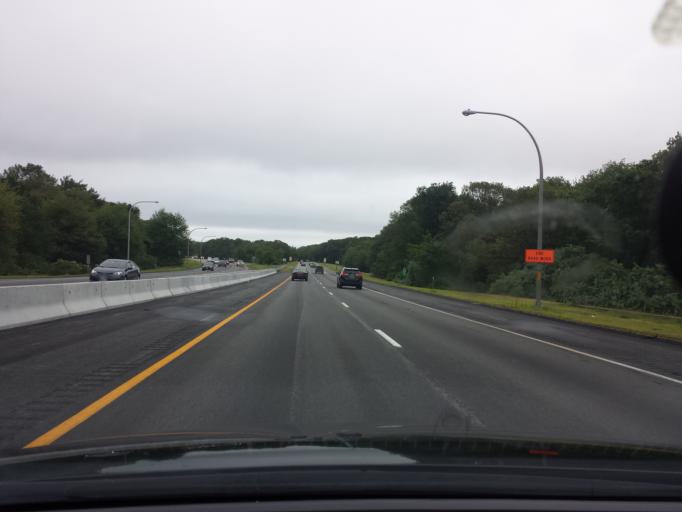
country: US
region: Rhode Island
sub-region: Kent County
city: West Warwick
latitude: 41.6666
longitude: -71.4969
